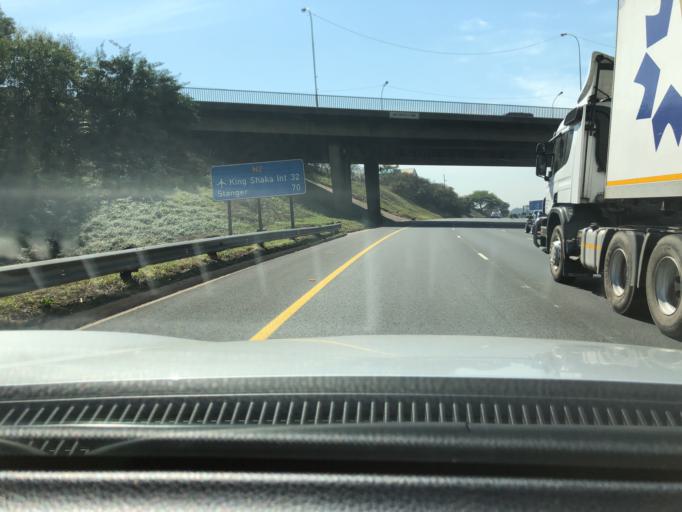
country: ZA
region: KwaZulu-Natal
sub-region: eThekwini Metropolitan Municipality
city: Berea
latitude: -29.8311
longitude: 30.9608
